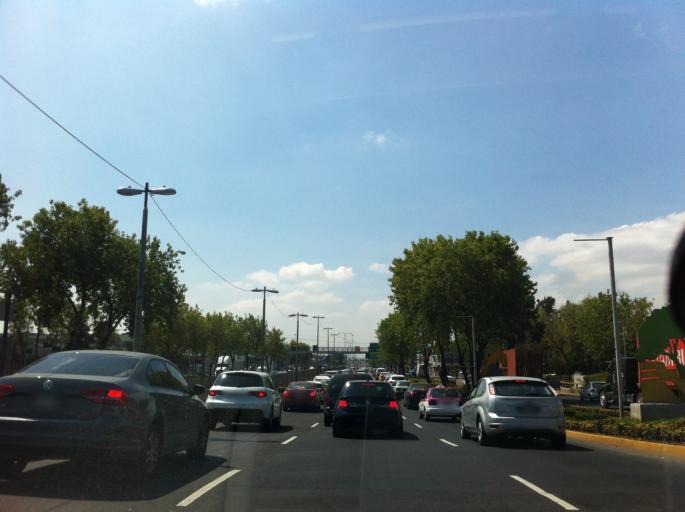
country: MX
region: Mexico City
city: Venustiano Carranza
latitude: 19.4269
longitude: -99.0925
